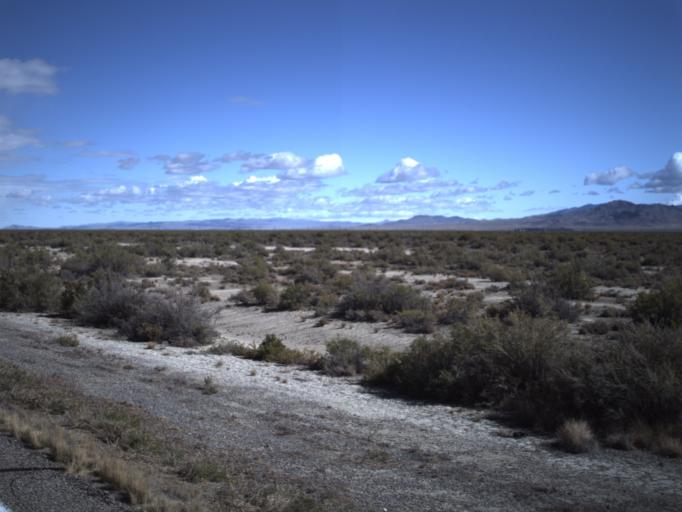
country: US
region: Nevada
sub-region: White Pine County
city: McGill
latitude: 39.0475
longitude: -114.0363
